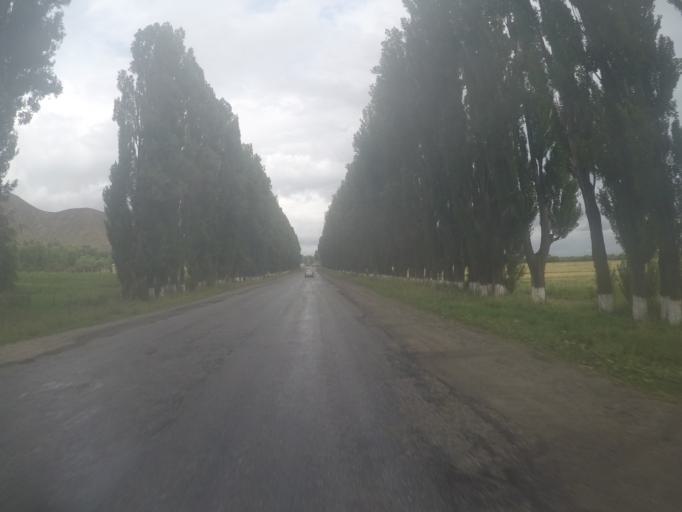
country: KG
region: Ysyk-Koel
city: Tyup
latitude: 42.7451
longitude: 78.0769
